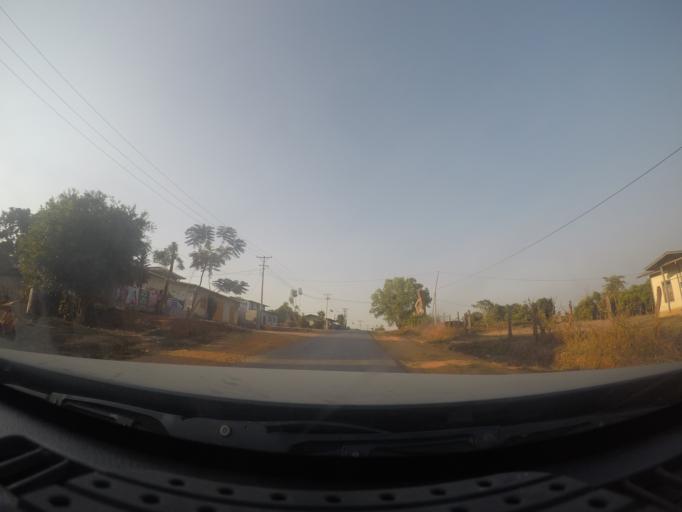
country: MM
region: Shan
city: Taunggyi
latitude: 20.4532
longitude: 97.1311
